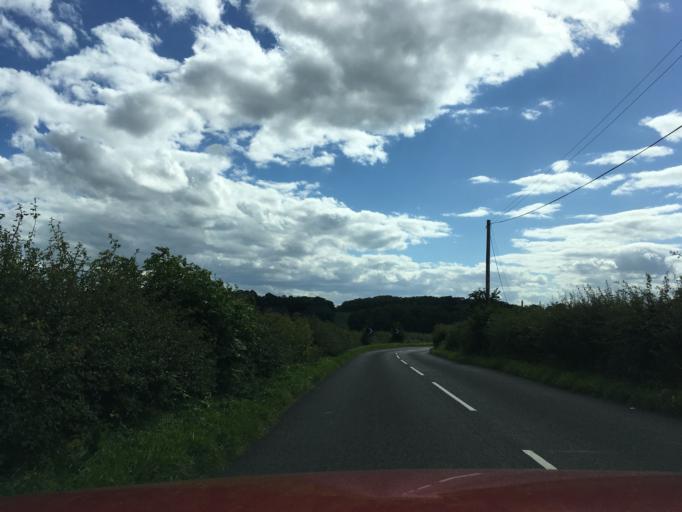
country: GB
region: England
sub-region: Nottinghamshire
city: East Leake
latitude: 52.8242
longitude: -1.1980
